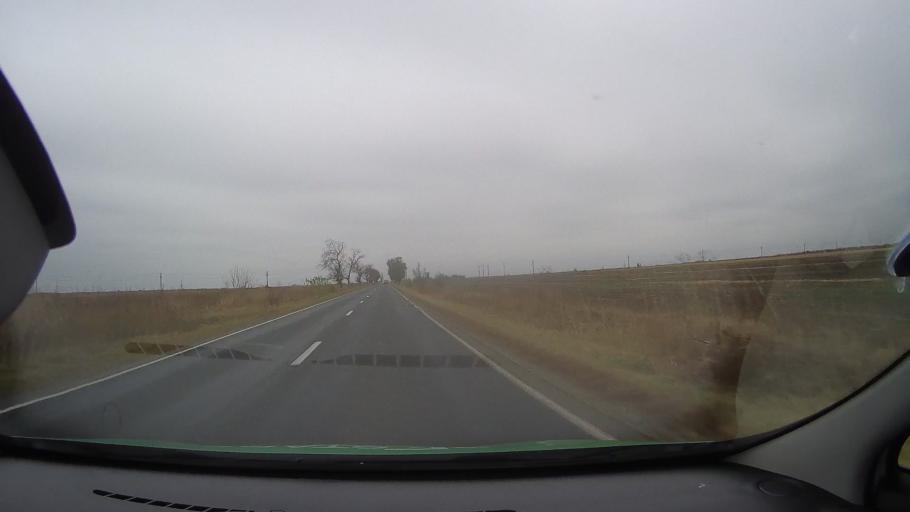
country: RO
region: Ialomita
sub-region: Comuna Scanteia
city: Scanteia
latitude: 44.7687
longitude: 27.4708
